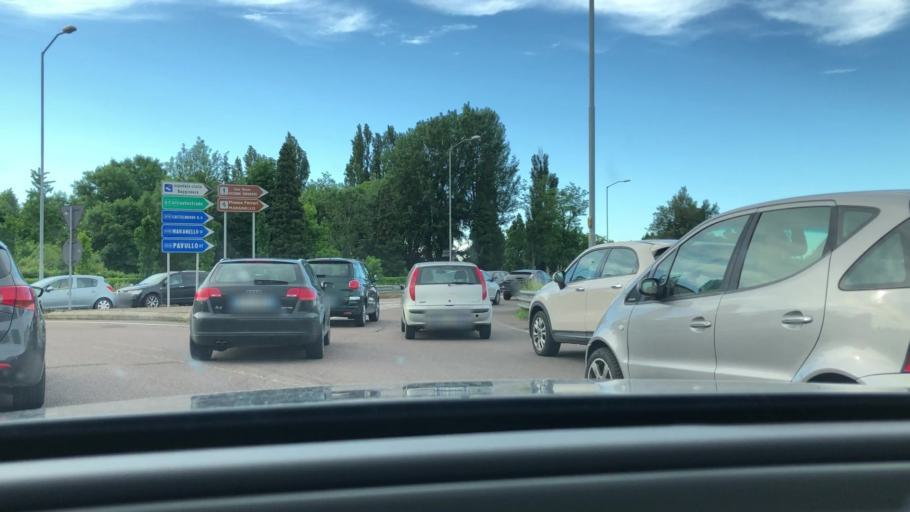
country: IT
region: Emilia-Romagna
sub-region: Provincia di Modena
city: Modena
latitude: 44.6107
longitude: 10.9357
